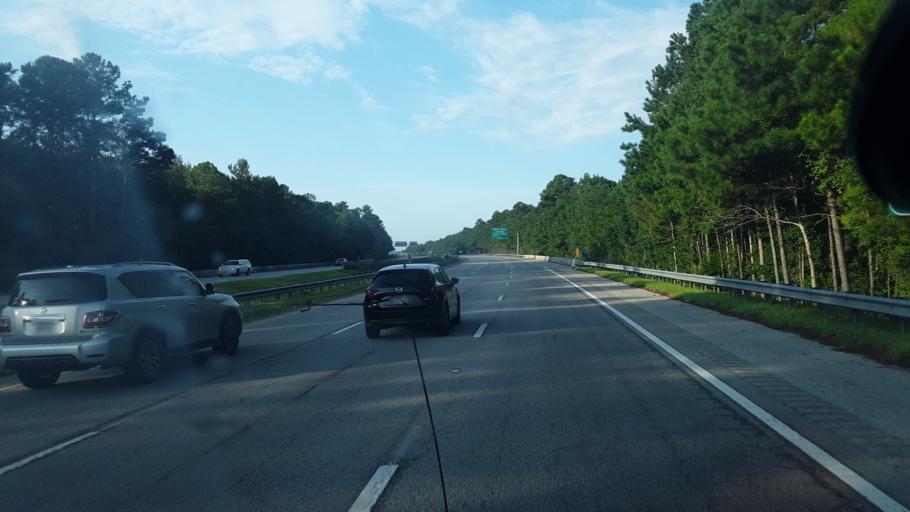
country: US
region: South Carolina
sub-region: Horry County
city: North Myrtle Beach
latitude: 33.8659
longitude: -78.6934
